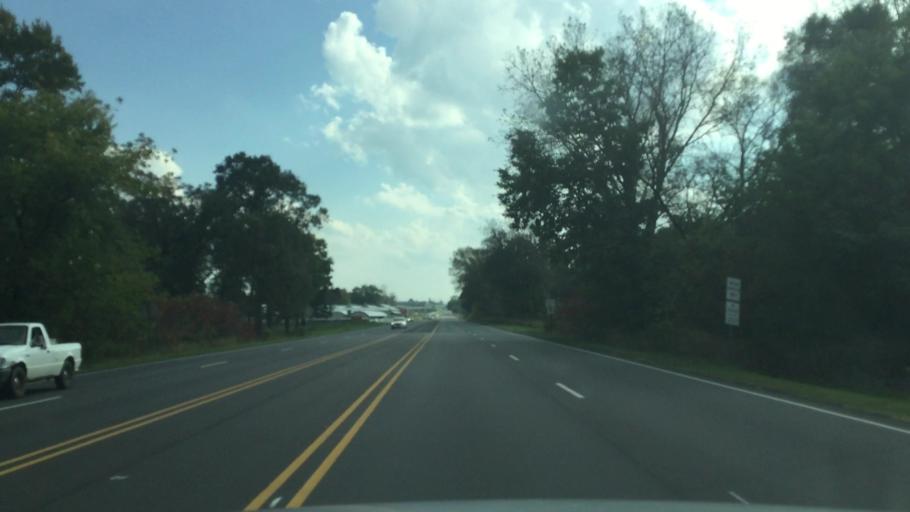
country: US
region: Michigan
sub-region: Kalamazoo County
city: Eastwood
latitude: 42.2821
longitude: -85.5308
